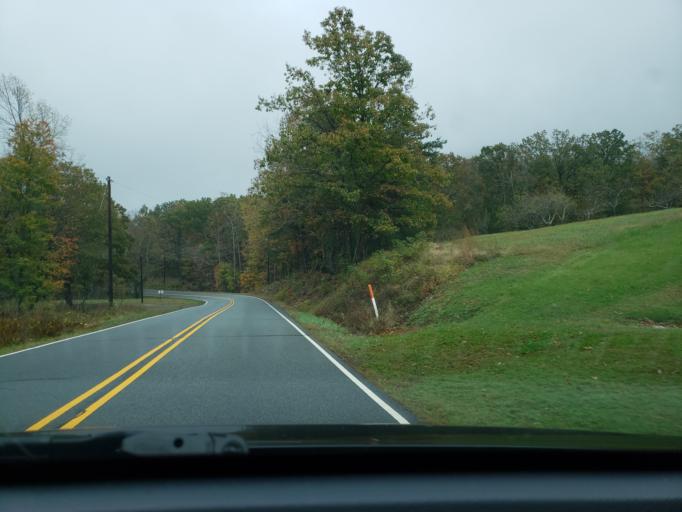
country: US
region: North Carolina
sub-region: Stokes County
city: Danbury
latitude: 36.4147
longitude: -80.2405
